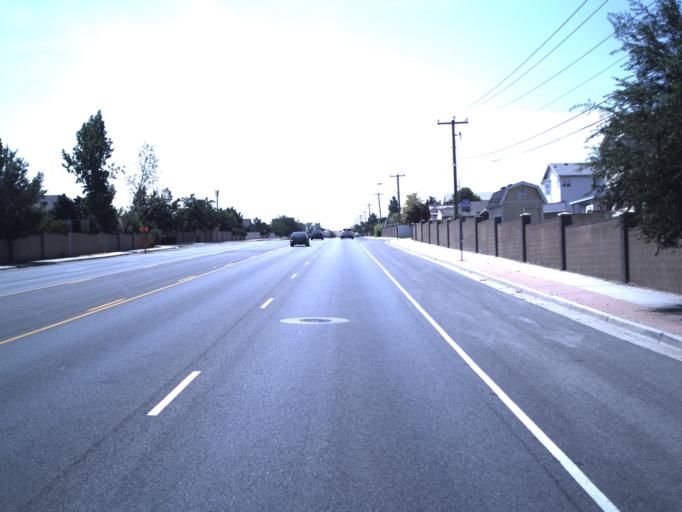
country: US
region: Utah
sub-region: Salt Lake County
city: West Valley City
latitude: 40.6756
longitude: -112.0248
